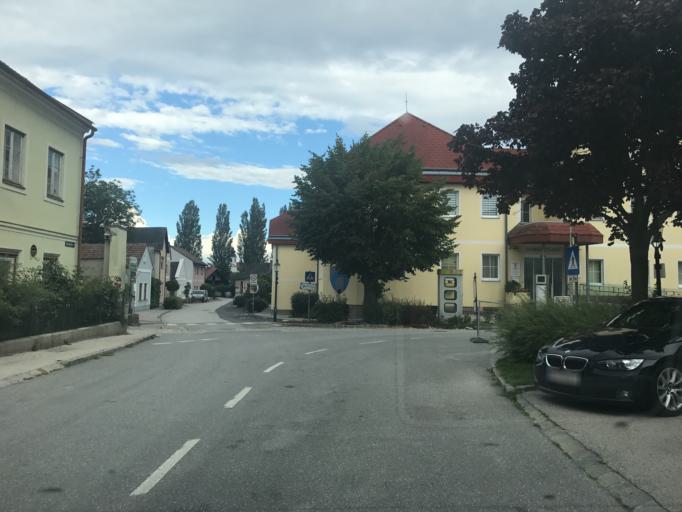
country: AT
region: Lower Austria
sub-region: Politischer Bezirk Wiener Neustadt
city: Markt Piesting
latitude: 47.8655
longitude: 16.1686
